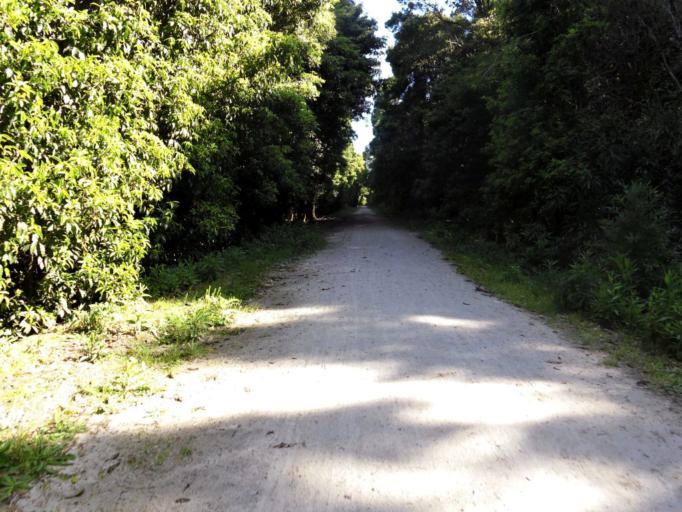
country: AU
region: Victoria
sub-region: Latrobe
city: Morwell
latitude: -38.6788
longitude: 146.1595
